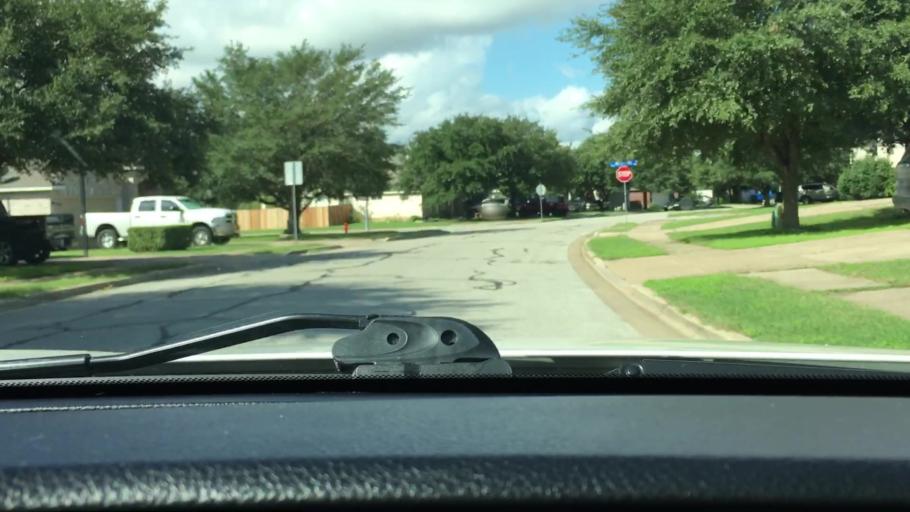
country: US
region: Texas
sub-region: Travis County
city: Windemere
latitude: 30.4760
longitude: -97.6454
